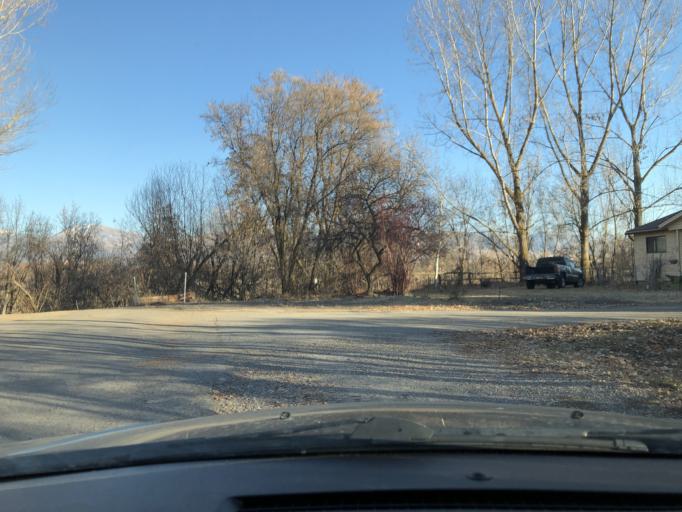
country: US
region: Utah
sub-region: Cache County
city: Wellsville
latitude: 41.6449
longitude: -111.9265
